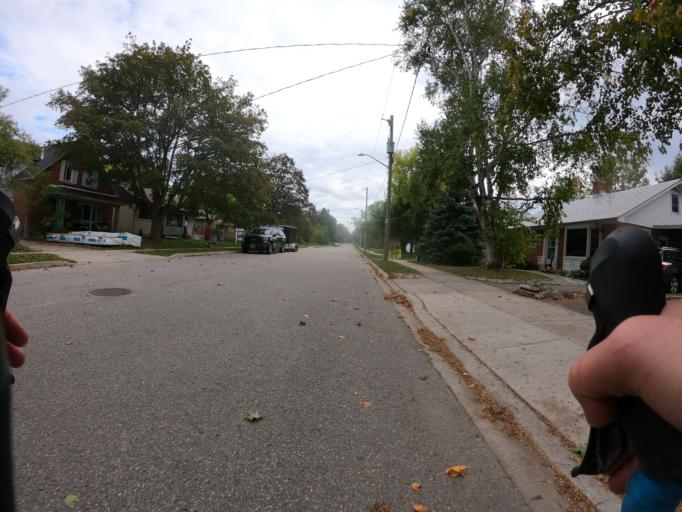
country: CA
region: Ontario
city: Waterloo
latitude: 43.4599
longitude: -80.5334
